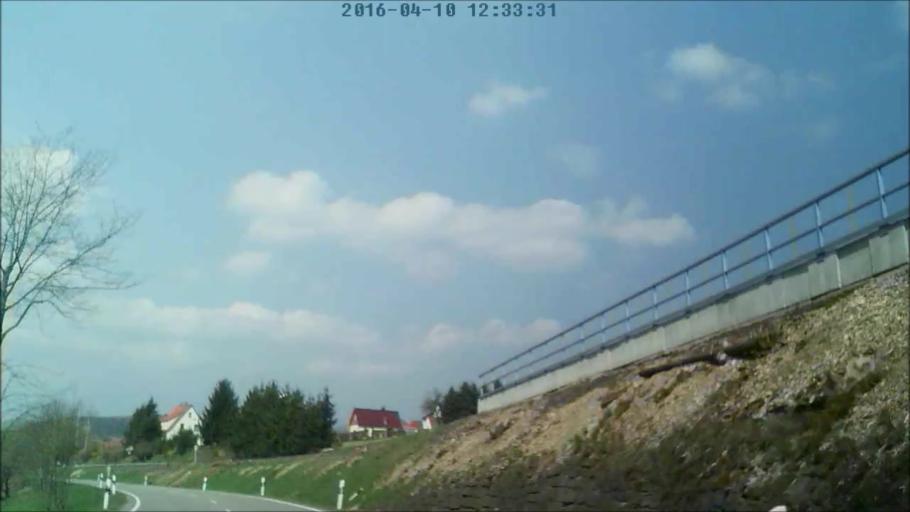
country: DE
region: Thuringia
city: Breitenbach
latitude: 50.7066
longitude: 10.4806
